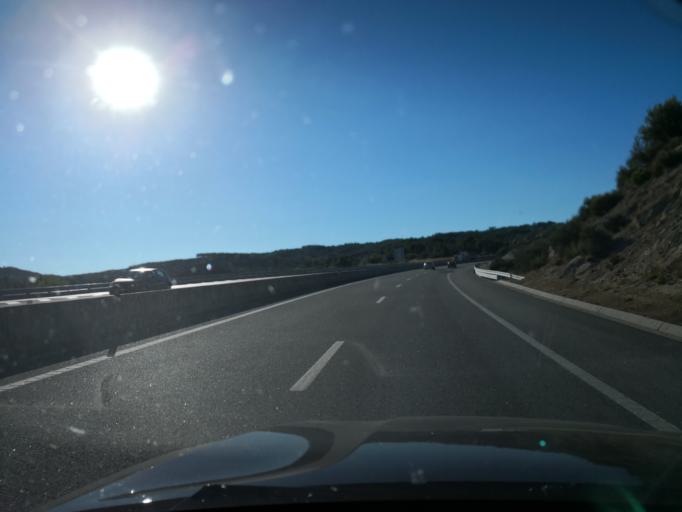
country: PT
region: Vila Real
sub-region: Murca
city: Murca
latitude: 41.3883
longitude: -7.4649
